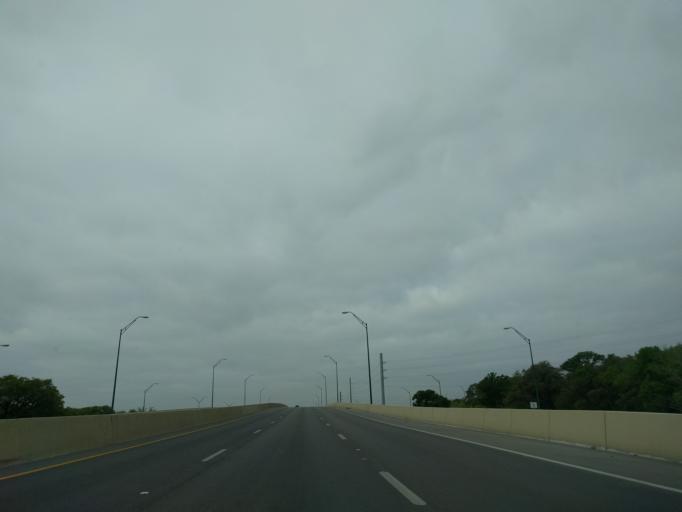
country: US
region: Texas
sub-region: Bexar County
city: Alamo Heights
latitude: 29.5464
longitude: -98.4525
